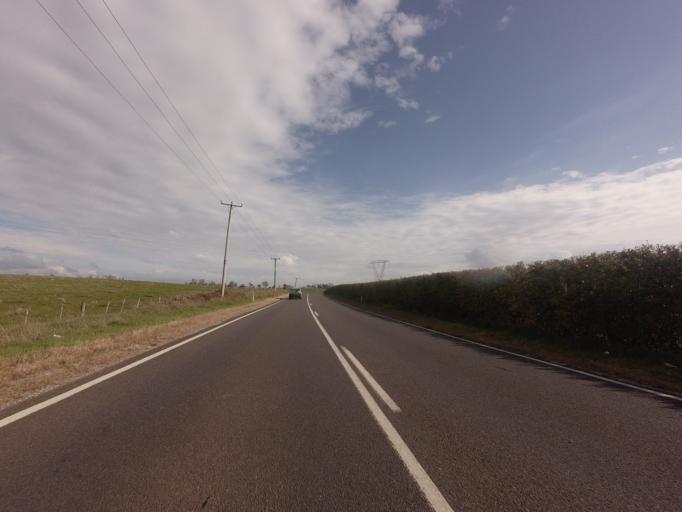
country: AU
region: Tasmania
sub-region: Meander Valley
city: Deloraine
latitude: -41.5241
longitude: 146.7148
